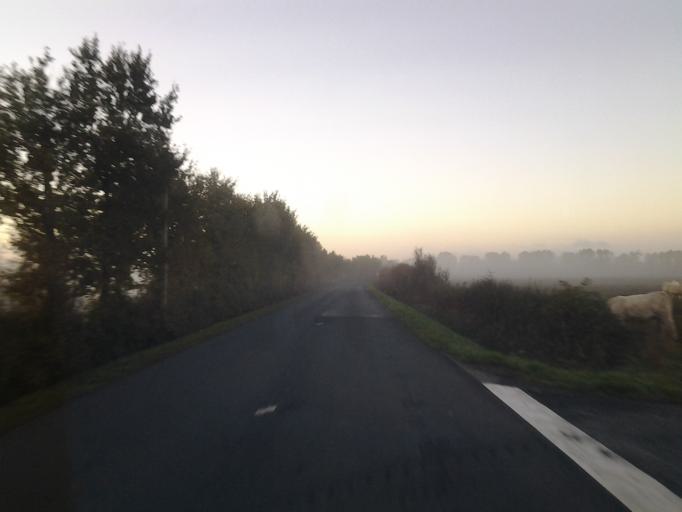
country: FR
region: Pays de la Loire
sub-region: Departement de la Vendee
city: Bournezeau
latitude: 46.6437
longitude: -1.2319
